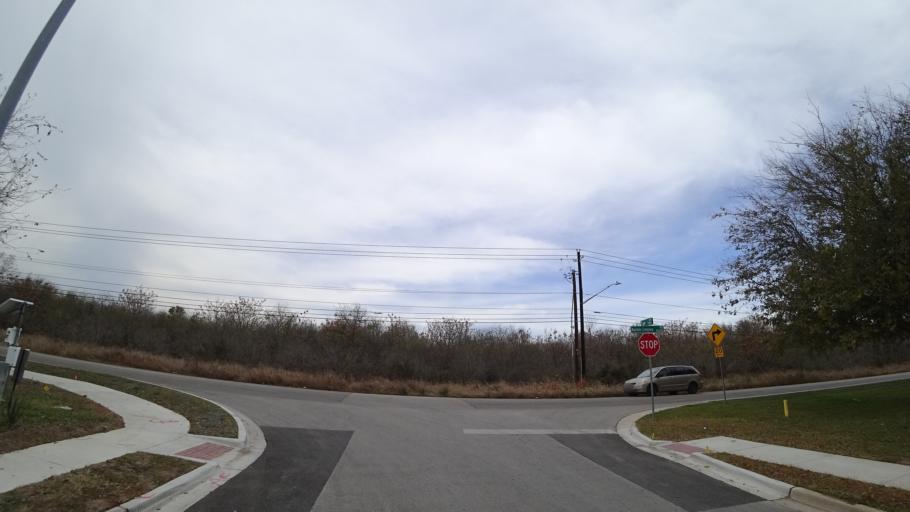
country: US
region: Texas
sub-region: Travis County
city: Onion Creek
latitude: 30.1592
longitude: -97.7514
